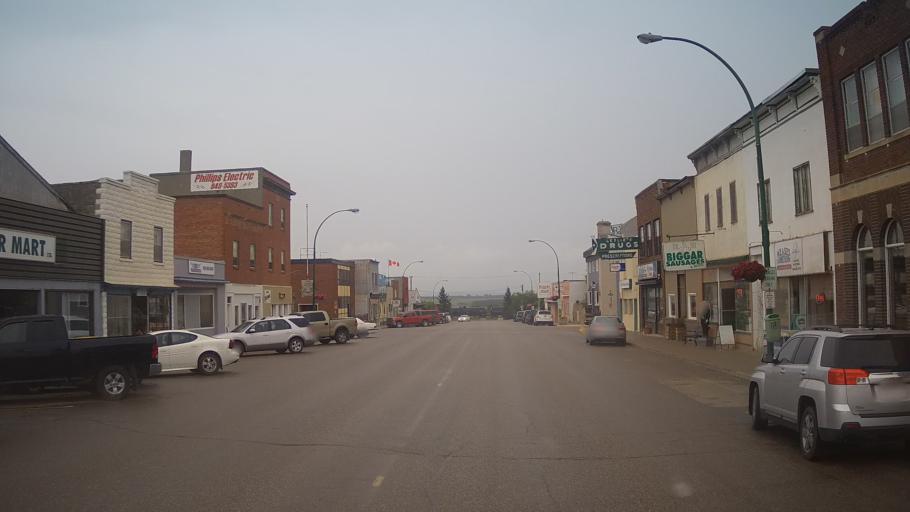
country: CA
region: Saskatchewan
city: Biggar
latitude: 52.0555
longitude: -107.9855
